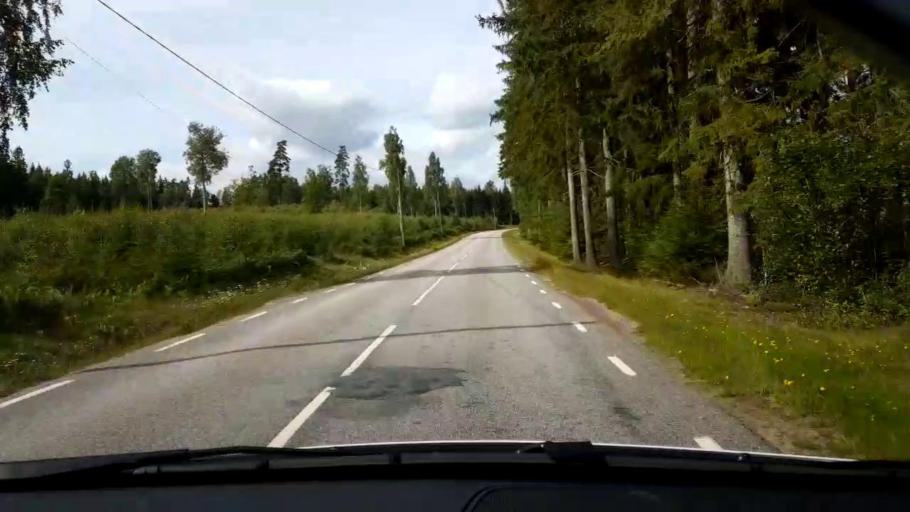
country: SE
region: Joenkoeping
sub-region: Vetlanda Kommun
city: Vetlanda
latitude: 57.3371
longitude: 15.0757
